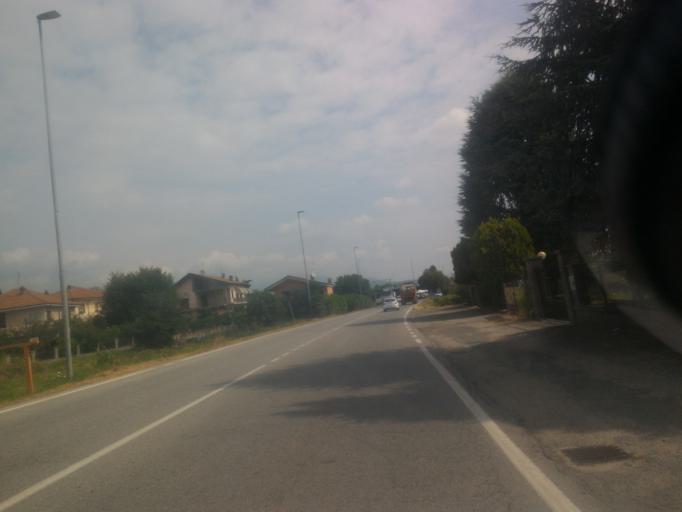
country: IT
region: Piedmont
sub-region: Provincia di Torino
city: Bricherasio
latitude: 44.8373
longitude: 7.3050
